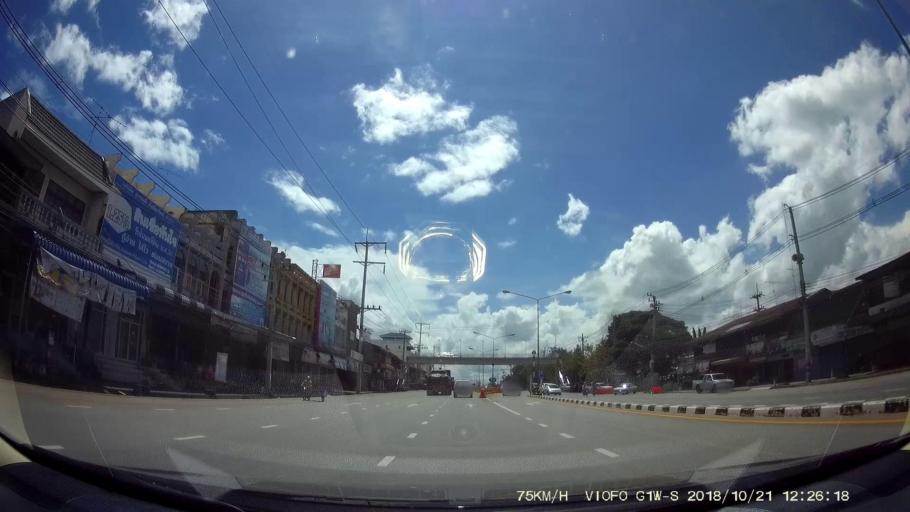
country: TH
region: Nakhon Ratchasima
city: Dan Khun Thot
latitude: 15.2111
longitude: 101.7681
